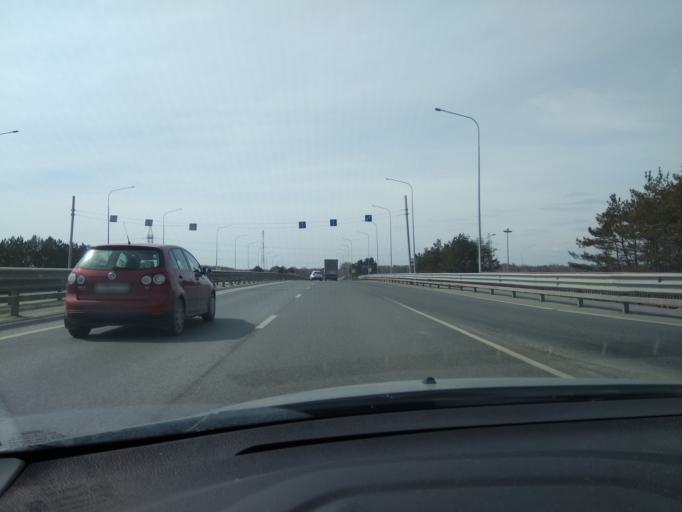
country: RU
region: Tjumen
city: Tyumen
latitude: 57.1302
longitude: 65.4823
